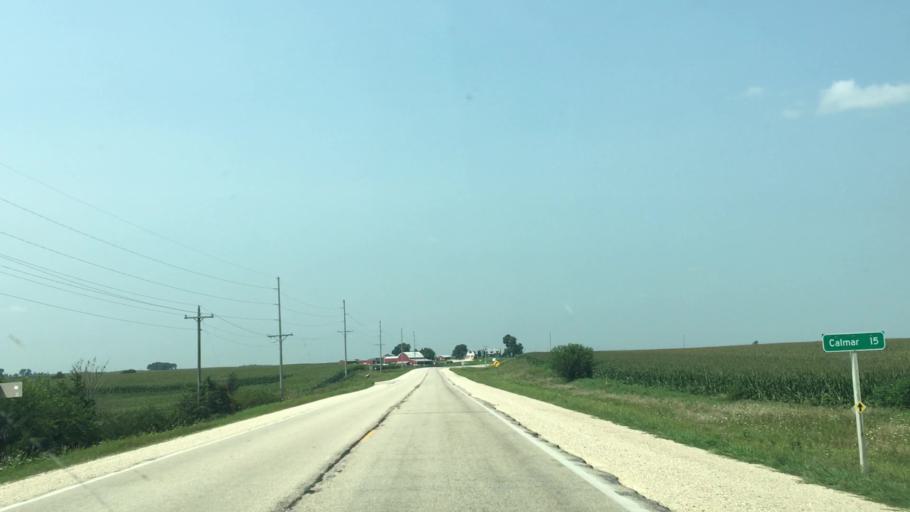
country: US
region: Iowa
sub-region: Fayette County
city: West Union
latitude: 42.9751
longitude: -91.8205
